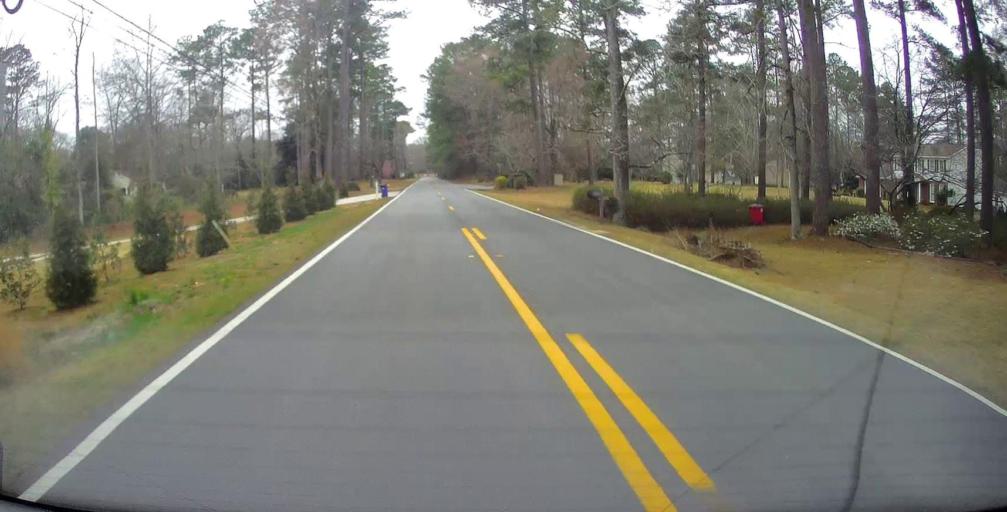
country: US
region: Georgia
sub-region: Bibb County
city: Macon
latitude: 32.9023
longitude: -83.7365
